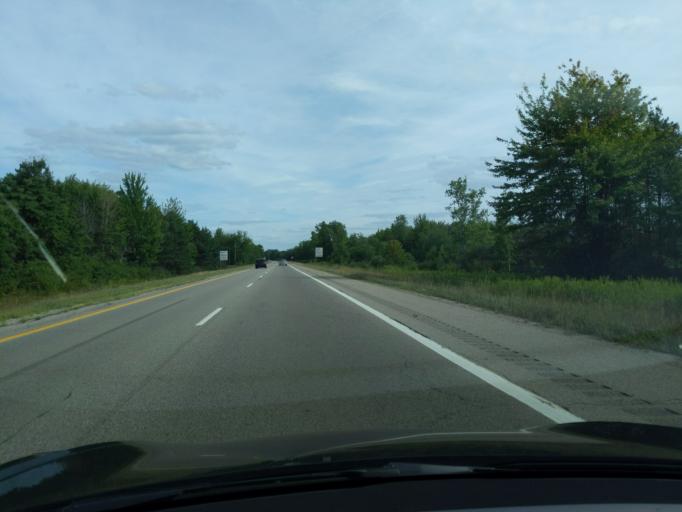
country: US
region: Michigan
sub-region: Muskegon County
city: Fruitport
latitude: 43.1067
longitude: -86.1173
